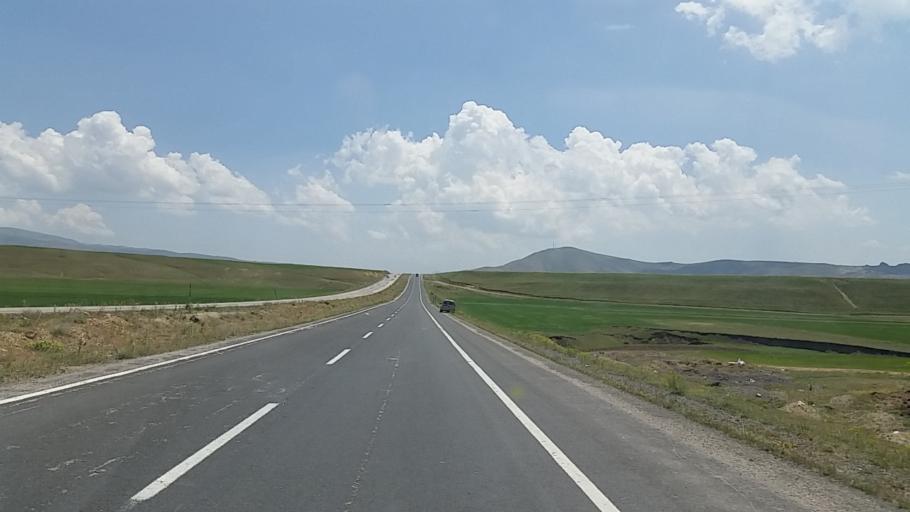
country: TR
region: Agri
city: Taslicay
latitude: 39.6277
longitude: 43.4462
